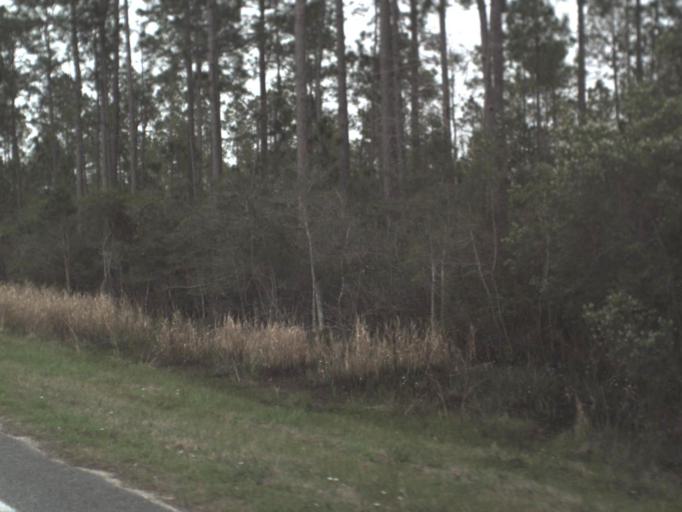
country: US
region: Florida
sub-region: Leon County
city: Woodville
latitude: 30.1981
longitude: -84.1600
